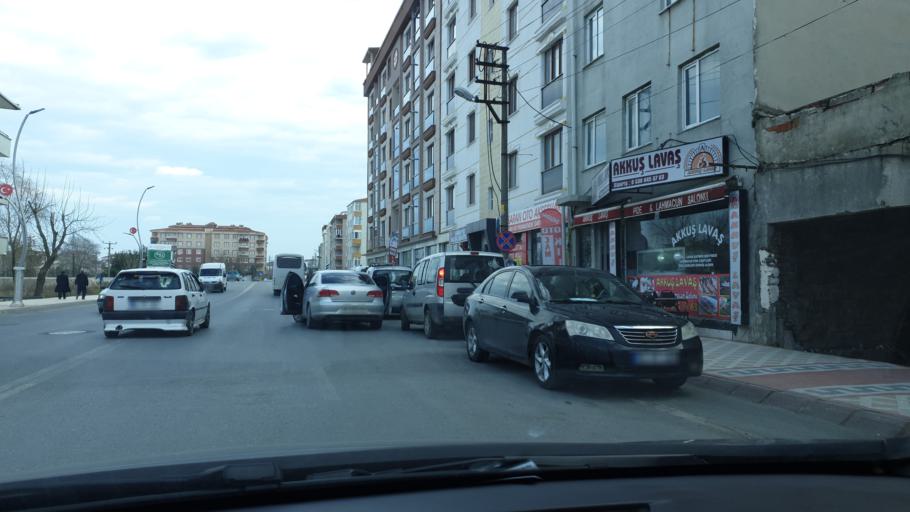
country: TR
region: Tekirdag
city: Cerkezkoey
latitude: 41.2817
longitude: 28.0022
